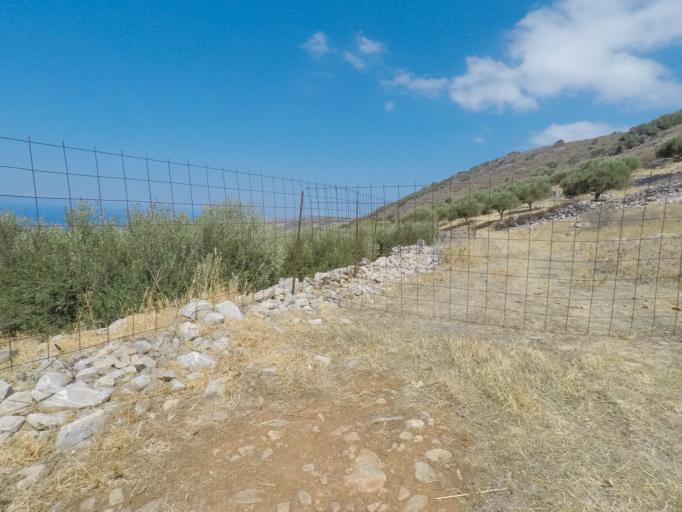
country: GR
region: Crete
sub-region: Nomos Lasithiou
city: Elounda
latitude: 35.3163
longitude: 25.6821
